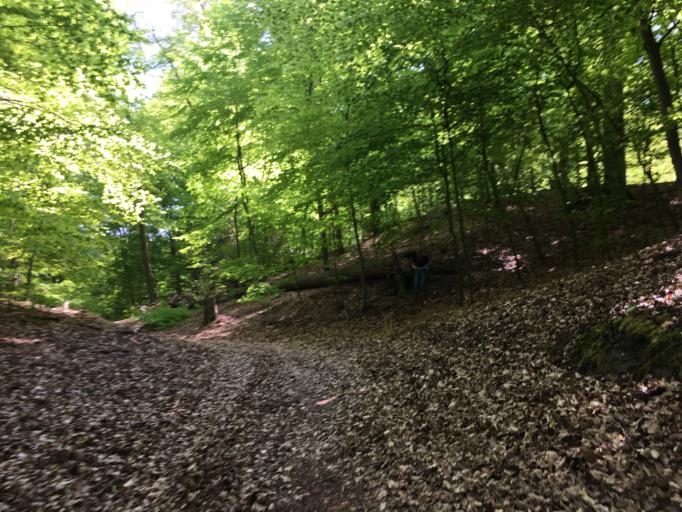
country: DE
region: Brandenburg
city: Wandlitz
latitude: 52.7480
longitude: 13.5259
